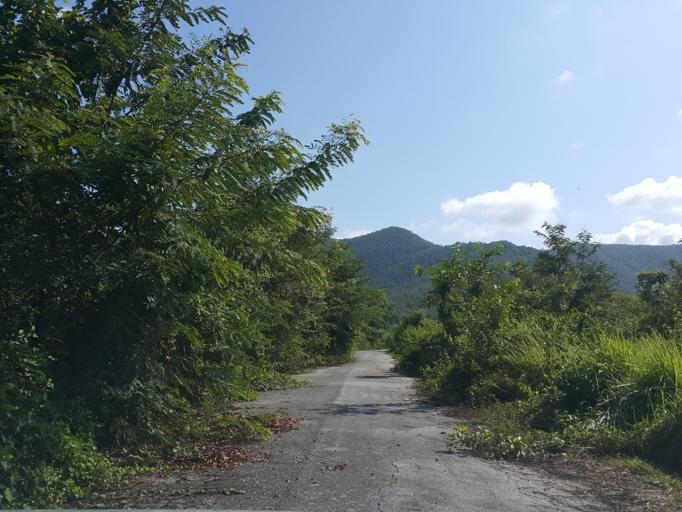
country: TH
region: Chiang Mai
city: Mae On
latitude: 18.8044
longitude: 99.1910
